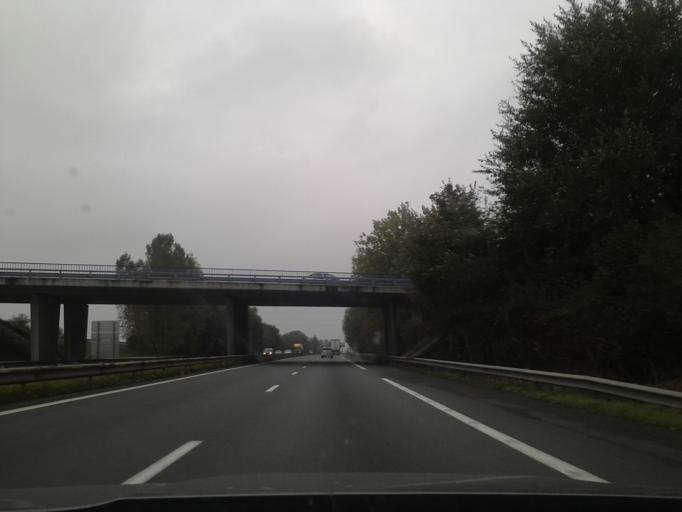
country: FR
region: Nord-Pas-de-Calais
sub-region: Departement du Nord
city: Neuville-sur-Escaut
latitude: 50.2912
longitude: 3.3597
